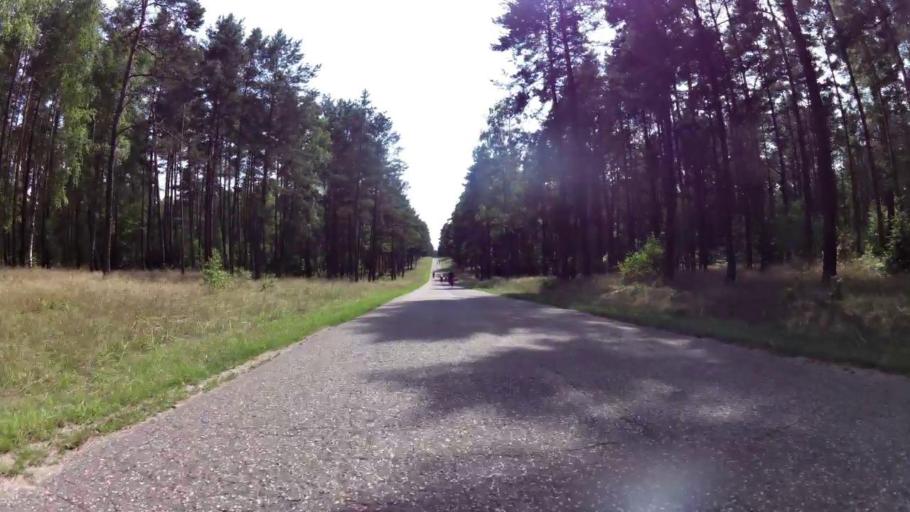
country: PL
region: West Pomeranian Voivodeship
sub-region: Powiat choszczenski
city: Drawno
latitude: 53.3267
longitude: 15.6923
